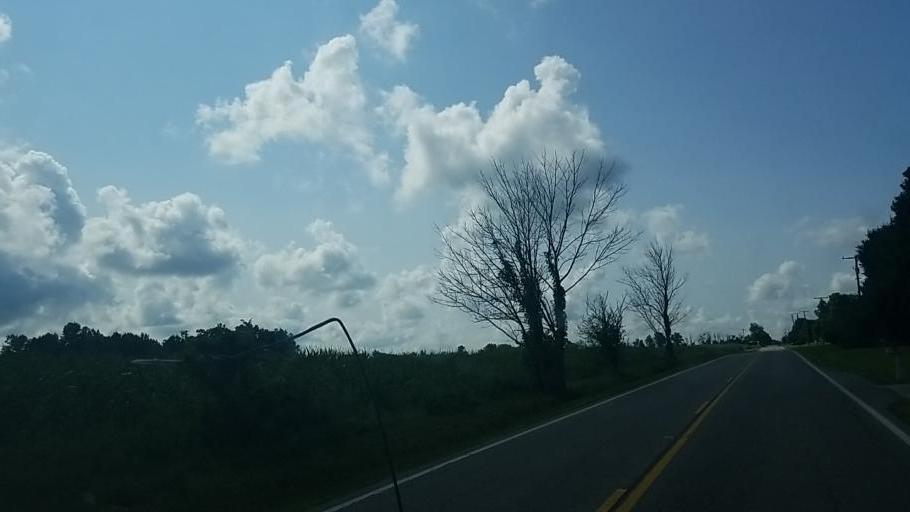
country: US
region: Ohio
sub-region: Ashland County
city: Ashland
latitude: 40.7685
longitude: -82.3067
